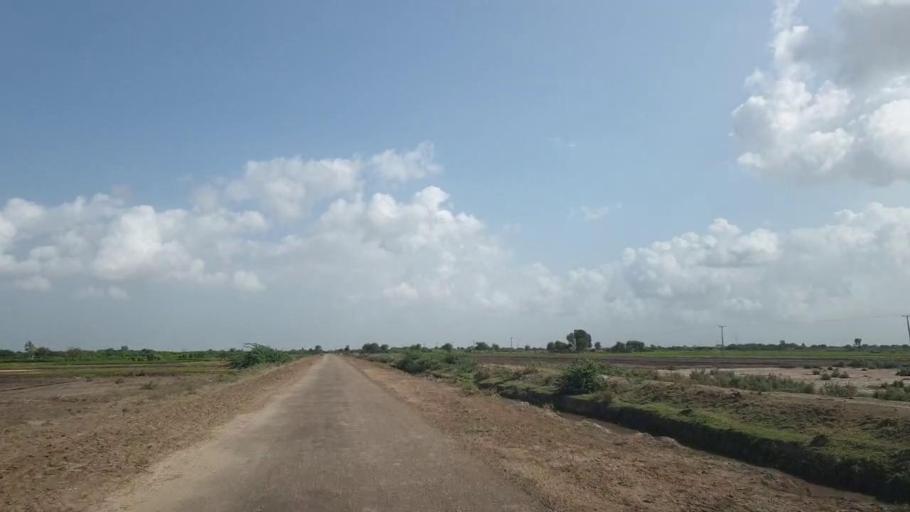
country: PK
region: Sindh
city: Kadhan
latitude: 24.5684
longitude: 69.0675
